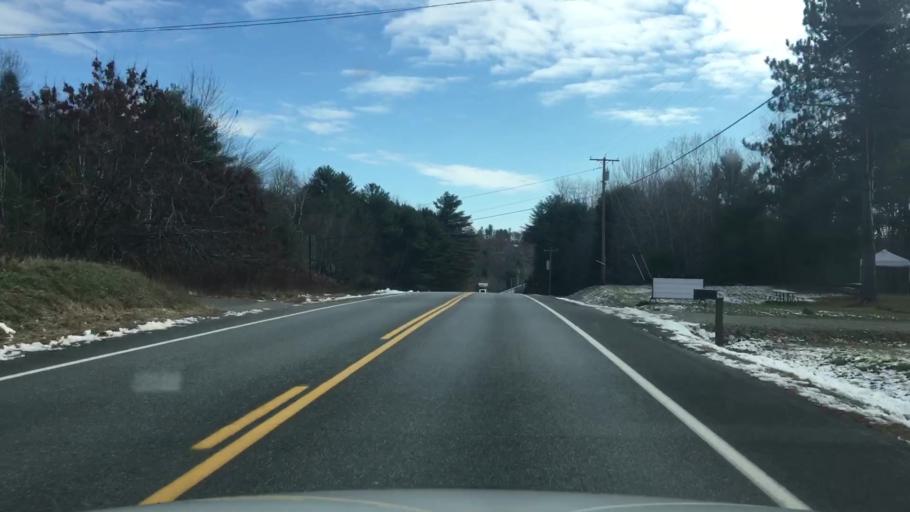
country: US
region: Maine
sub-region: Kennebec County
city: Wayne
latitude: 44.3409
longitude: -70.0246
